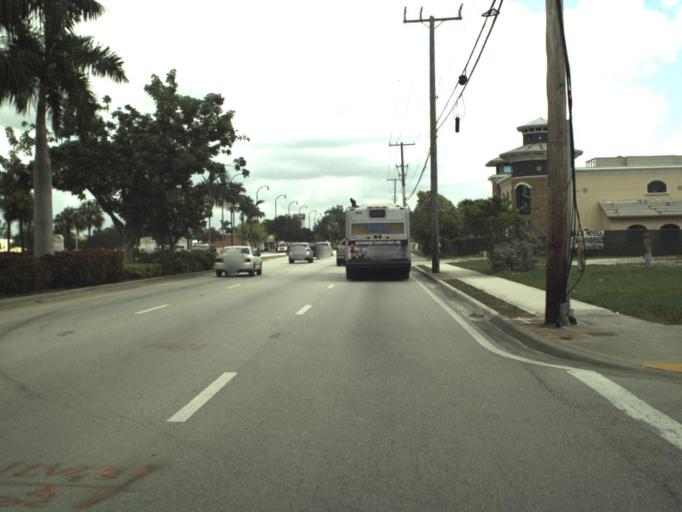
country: US
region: Florida
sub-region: Broward County
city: Lauderhill
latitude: 26.1423
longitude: -80.2026
